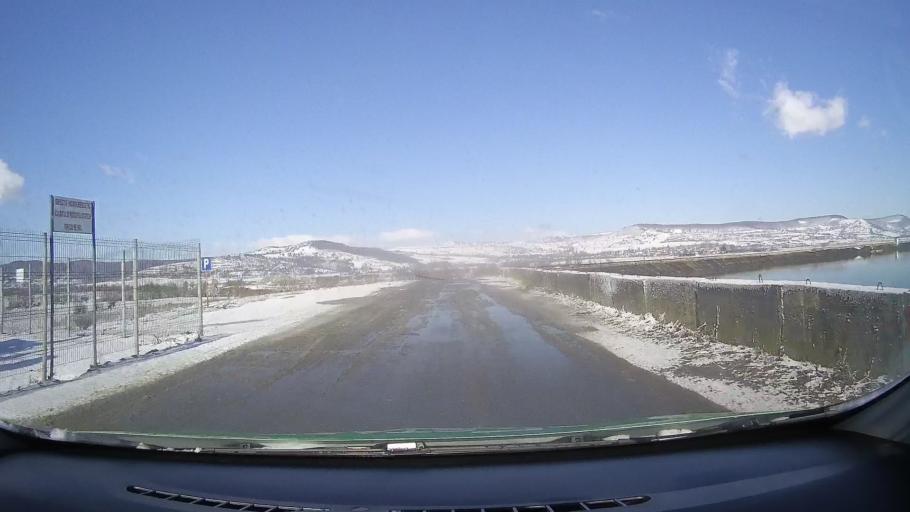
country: RO
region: Sibiu
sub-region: Comuna Avrig
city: Avrig
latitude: 45.7437
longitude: 24.3897
